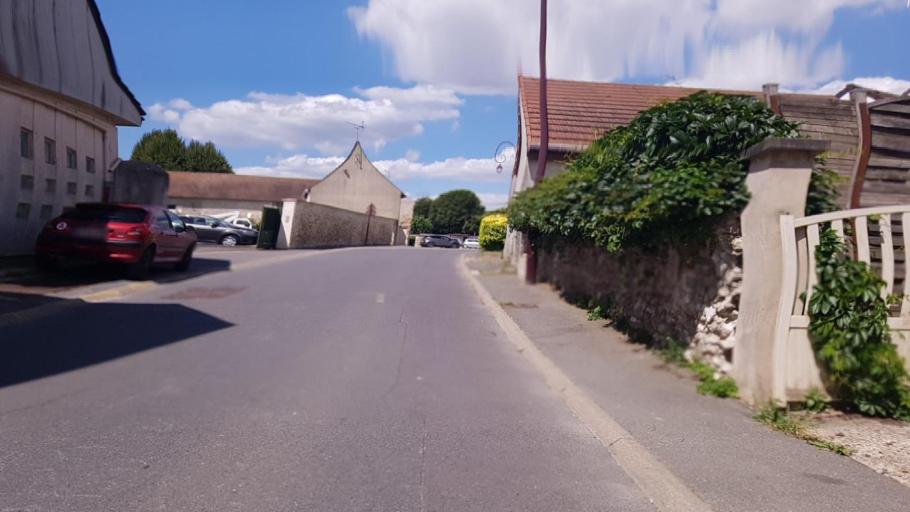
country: FR
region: Ile-de-France
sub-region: Departement de Seine-et-Marne
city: Moussy-le-Vieux
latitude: 49.0326
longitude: 2.6392
